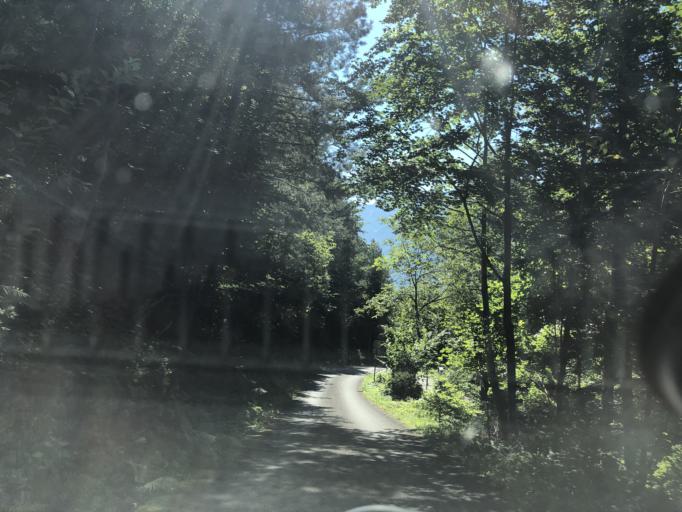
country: CH
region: Uri
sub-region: Uri
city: Flueelen
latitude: 46.9028
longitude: 8.6326
